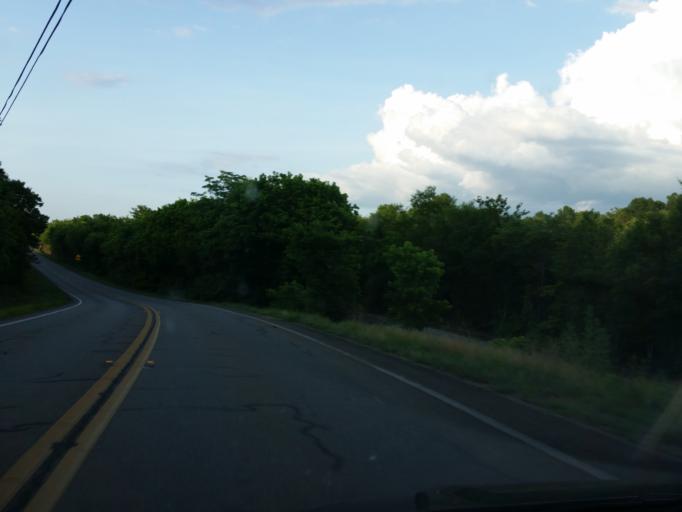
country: US
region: Georgia
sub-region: Dade County
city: Trenton
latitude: 34.9318
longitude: -85.4565
